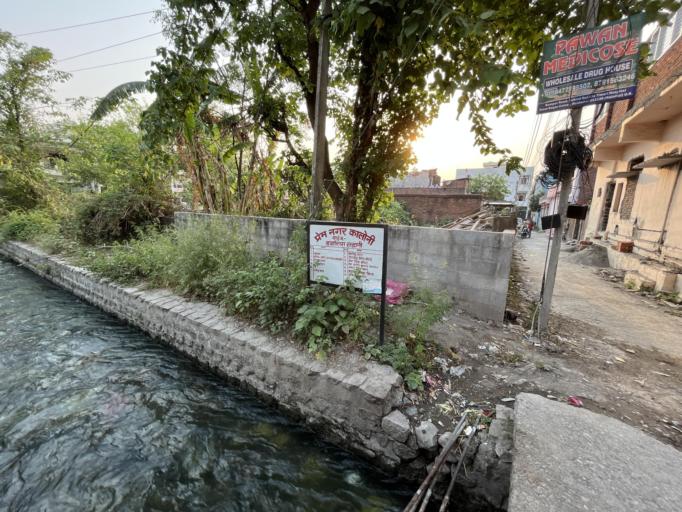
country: IN
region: Uttarakhand
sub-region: Naini Tal
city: Haldwani
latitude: 29.2033
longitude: 79.5142
